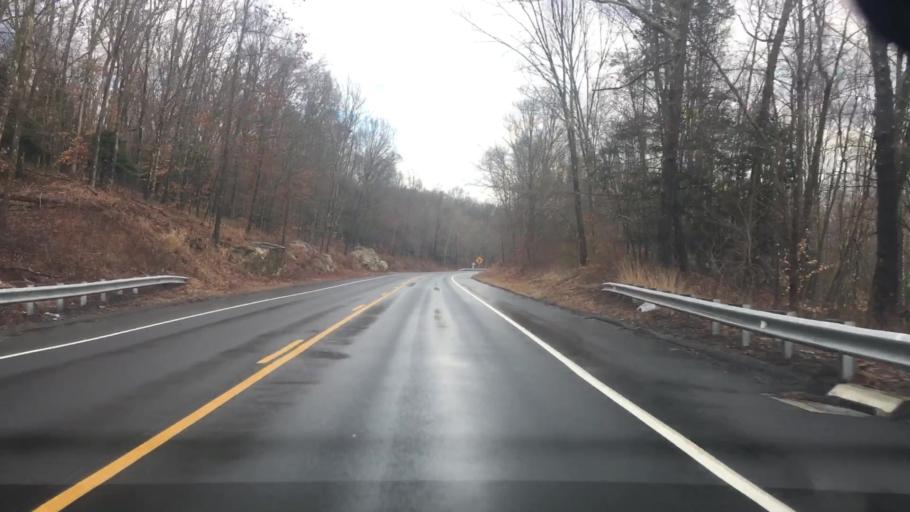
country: US
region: Connecticut
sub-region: Middlesex County
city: Higganum
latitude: 41.5269
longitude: -72.5667
